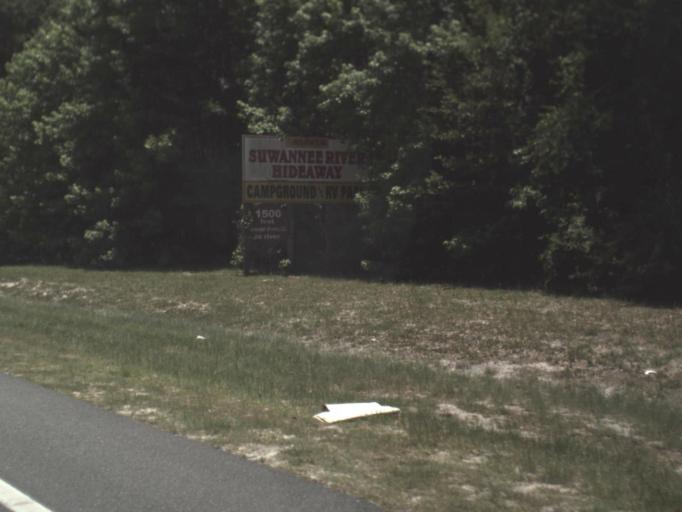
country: US
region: Florida
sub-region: Dixie County
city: Cross City
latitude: 29.6668
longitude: -82.9842
